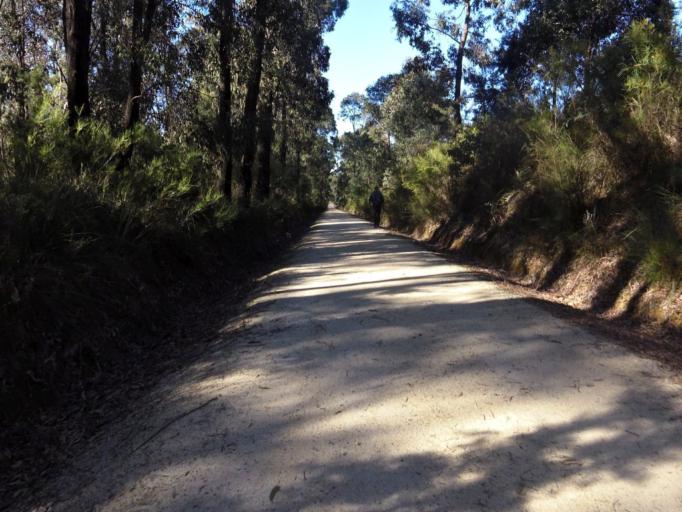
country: AU
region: Victoria
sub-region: Latrobe
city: Moe
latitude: -38.3752
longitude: 146.1980
